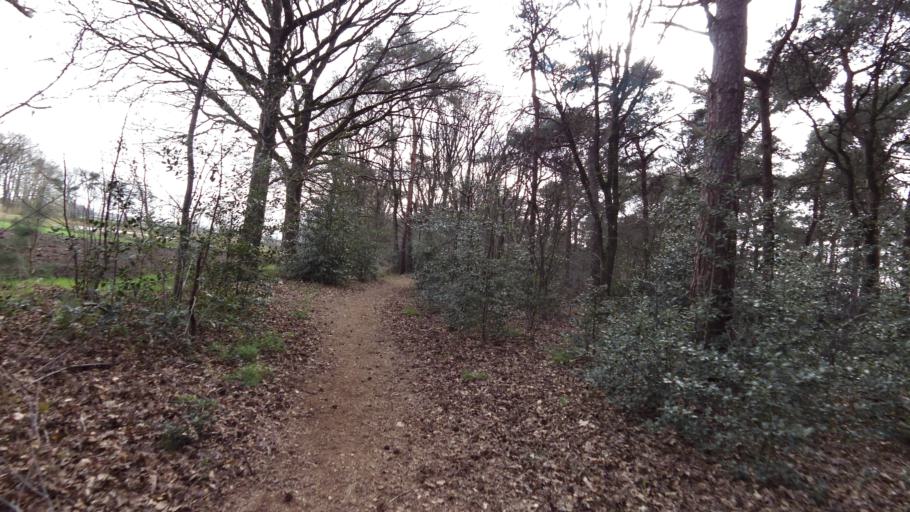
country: NL
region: Gelderland
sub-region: Gemeente Barneveld
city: Voorthuizen
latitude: 52.1931
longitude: 5.5756
